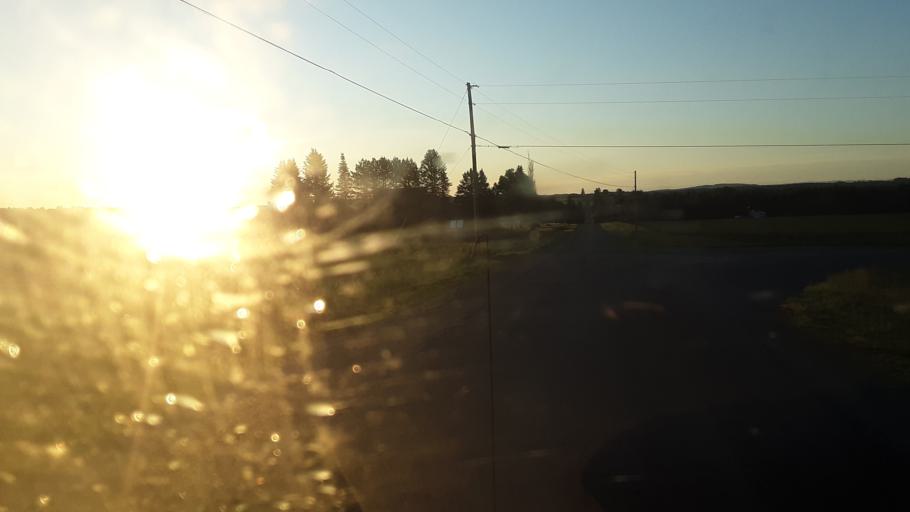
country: US
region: Maine
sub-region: Aroostook County
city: Caribou
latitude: 46.8029
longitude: -68.0985
